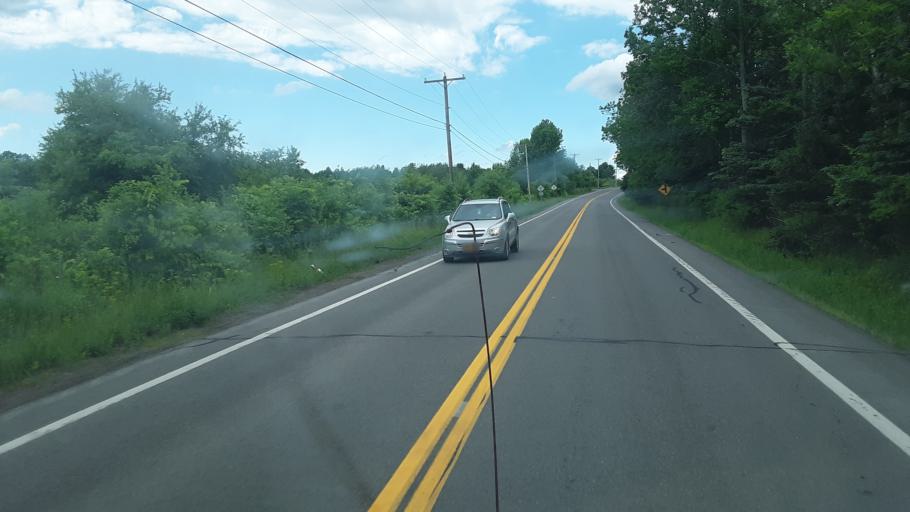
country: US
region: New York
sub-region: Oneida County
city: Rome
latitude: 43.3252
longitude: -75.4772
